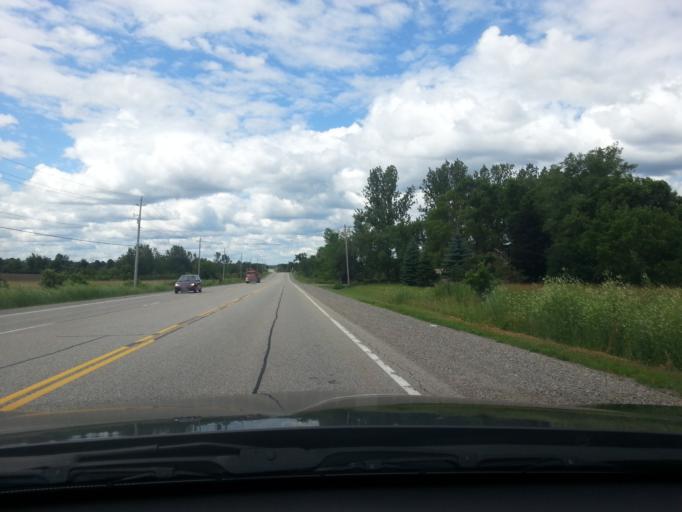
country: CA
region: Ontario
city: Perth
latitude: 44.7305
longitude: -76.1509
